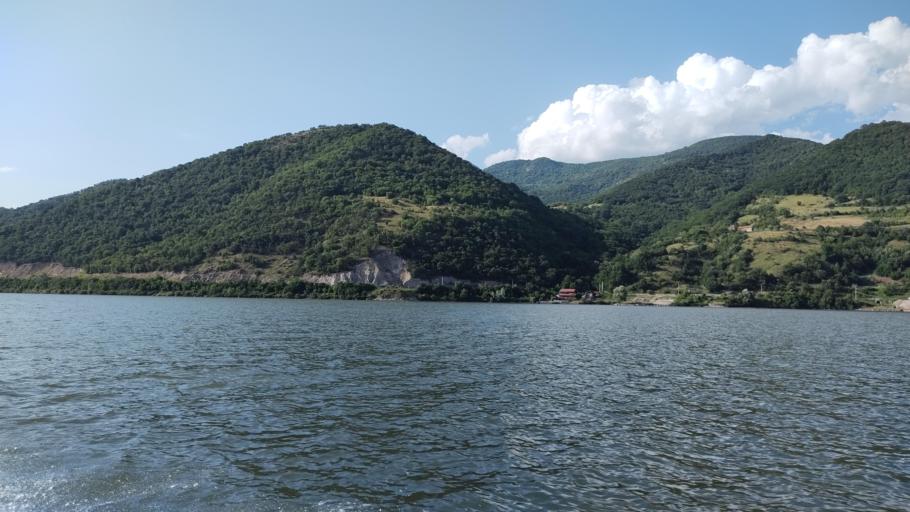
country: RO
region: Mehedinti
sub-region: Comuna Svinita
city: Svinita
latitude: 44.5388
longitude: 22.0555
